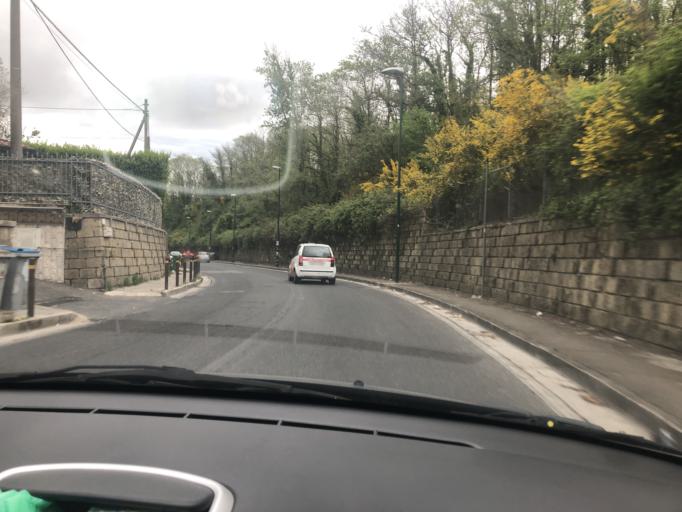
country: IT
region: Campania
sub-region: Provincia di Napoli
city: Torre Caracciolo
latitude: 40.8631
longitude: 14.2002
